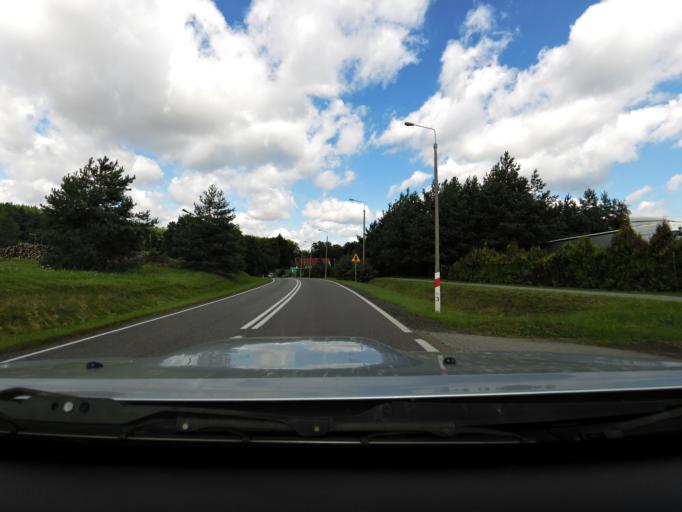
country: PL
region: Pomeranian Voivodeship
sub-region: Powiat kwidzynski
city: Ryjewo
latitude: 53.8014
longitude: 18.9640
